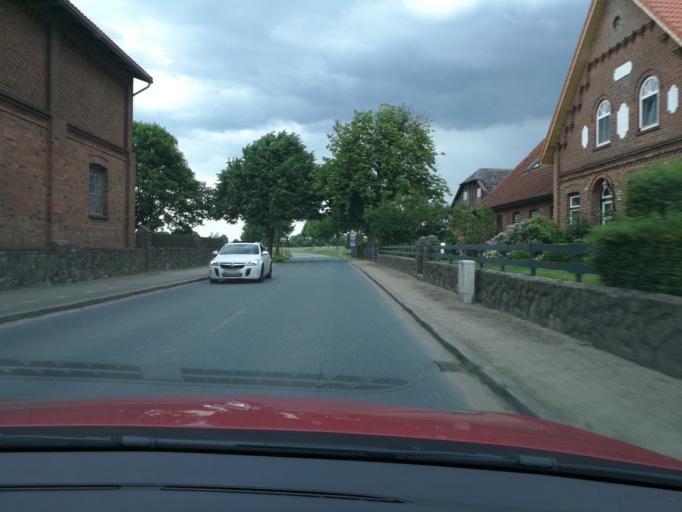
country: DE
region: Schleswig-Holstein
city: Lasbek
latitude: 53.7365
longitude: 10.3621
